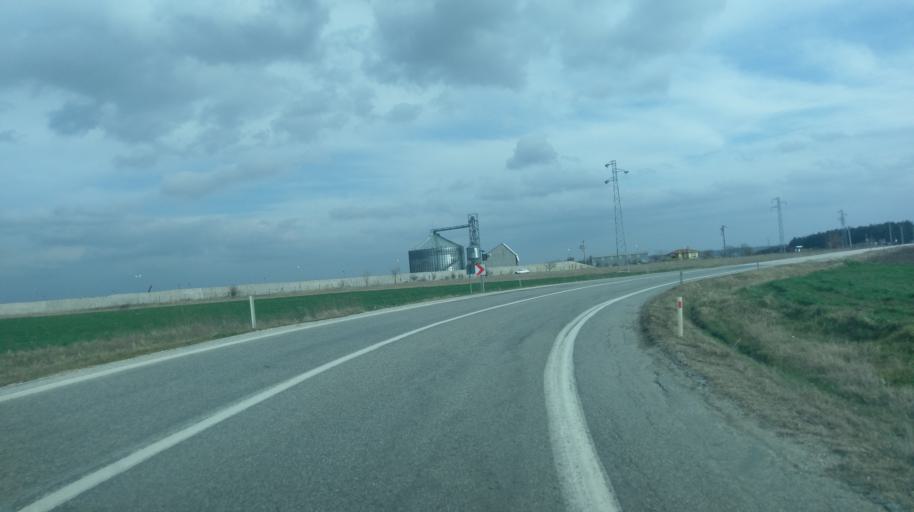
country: TR
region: Kirklareli
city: Inece
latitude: 41.6800
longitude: 27.0559
